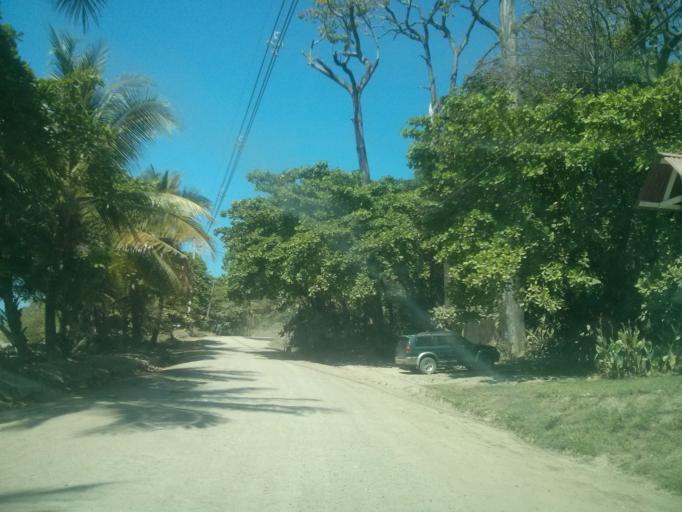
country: CR
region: Guanacaste
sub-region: Canton de Nandayure
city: Bejuco
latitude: 9.6588
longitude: -85.1845
